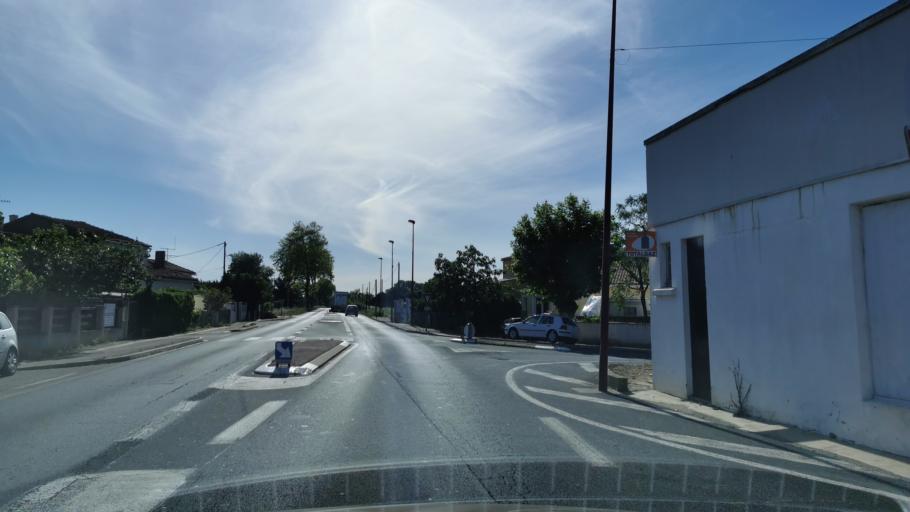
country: FR
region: Languedoc-Roussillon
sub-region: Departement de l'Aude
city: Canet
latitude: 43.2142
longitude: 2.8576
